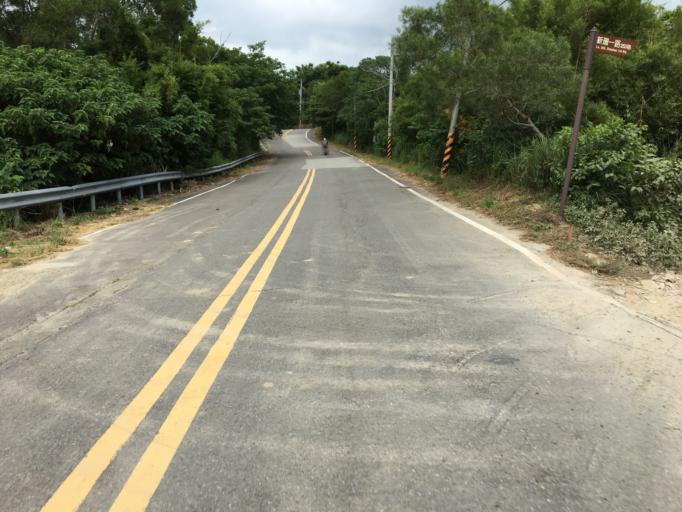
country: TW
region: Taiwan
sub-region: Hsinchu
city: Hsinchu
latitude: 24.7085
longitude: 120.9531
